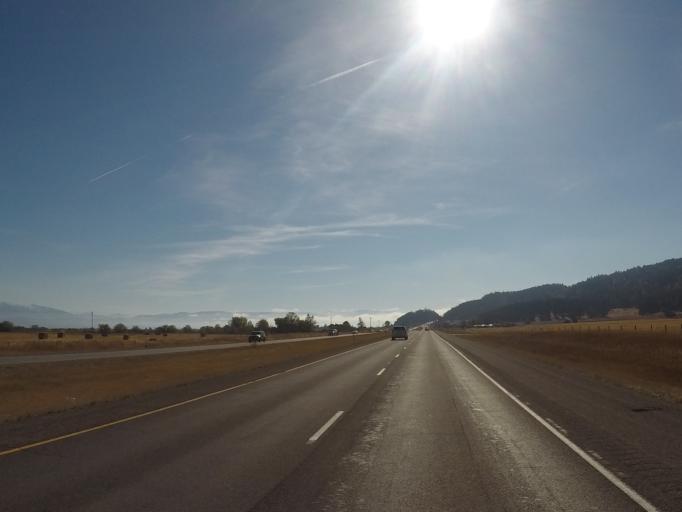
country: US
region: Montana
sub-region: Flathead County
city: Somers
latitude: 48.1090
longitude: -114.2487
